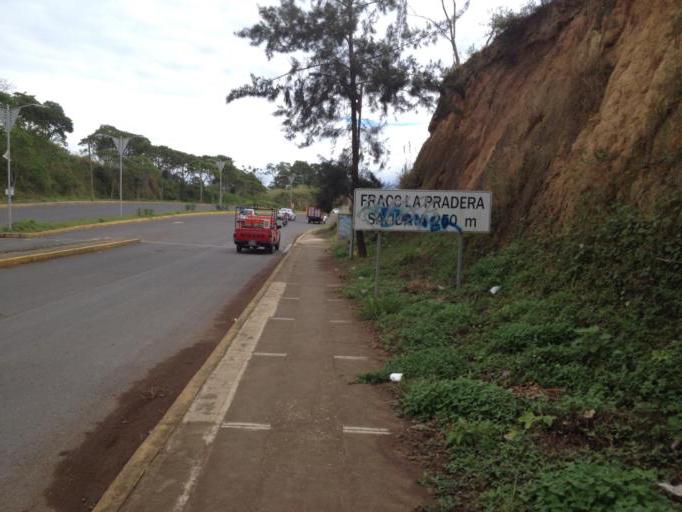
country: MX
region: Veracruz
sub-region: Emiliano Zapata
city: Las Trancas
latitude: 19.5040
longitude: -96.8604
